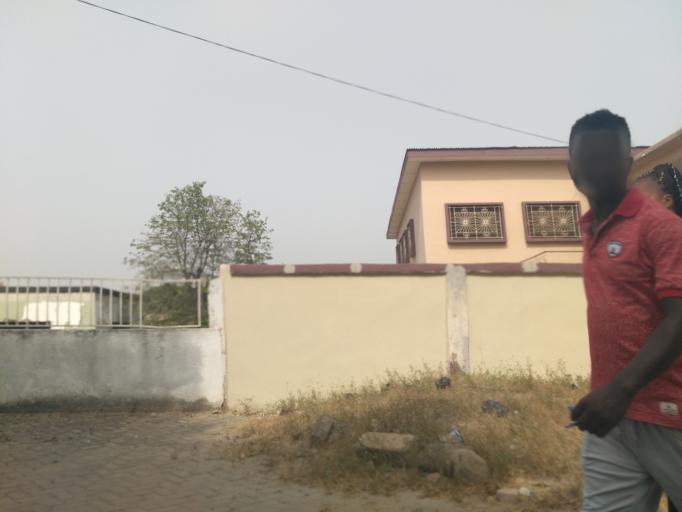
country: GH
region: Ashanti
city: Kumasi
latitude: 6.6795
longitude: -1.6000
